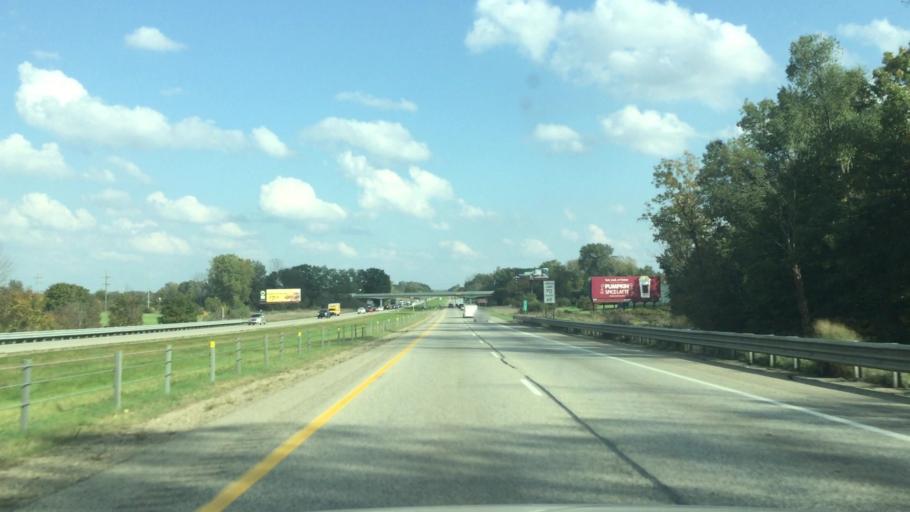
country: US
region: Michigan
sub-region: Calhoun County
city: Springfield
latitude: 42.2703
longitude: -85.2841
